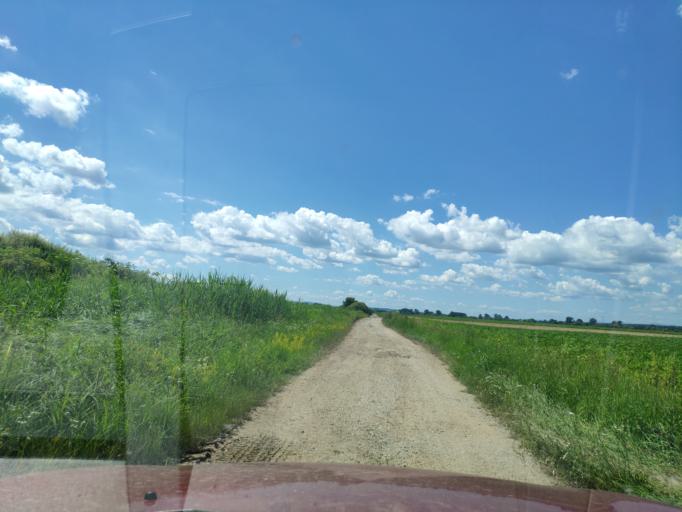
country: HU
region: Borsod-Abauj-Zemplen
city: Ozd
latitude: 48.2850
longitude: 20.2078
